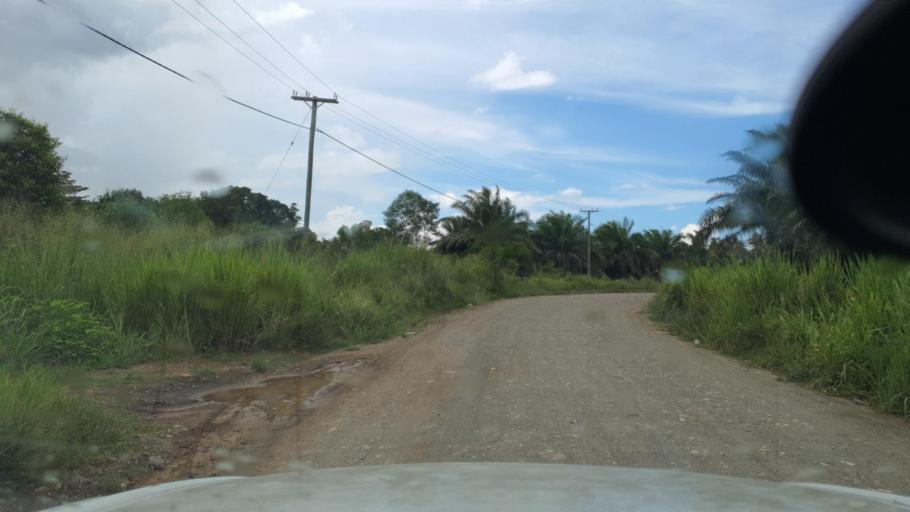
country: SB
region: Guadalcanal
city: Honiara
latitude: -9.4706
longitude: 160.1074
